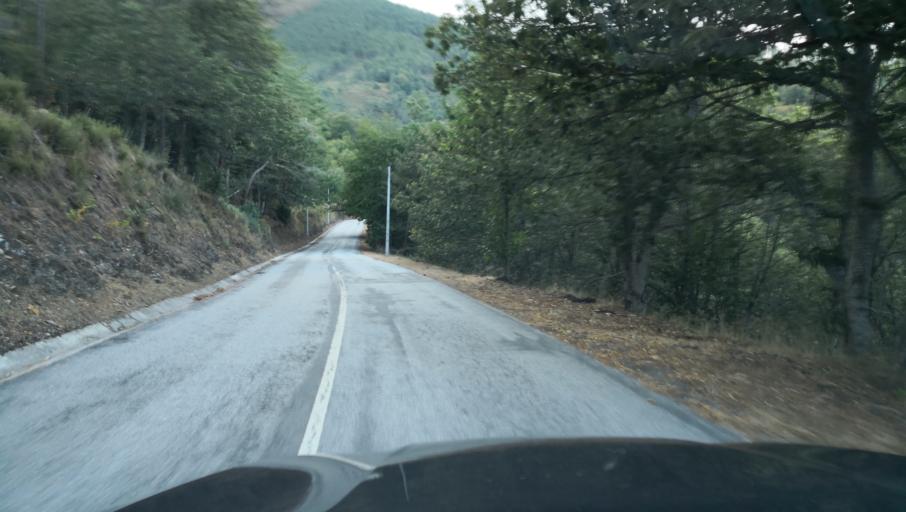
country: PT
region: Vila Real
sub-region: Santa Marta de Penaguiao
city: Santa Marta de Penaguiao
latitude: 41.2406
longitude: -7.8507
